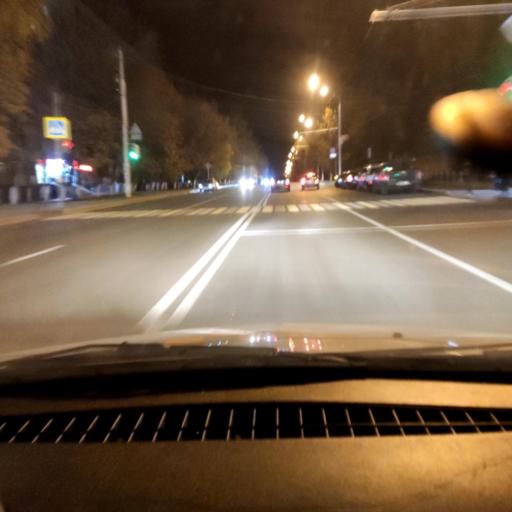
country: RU
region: Bashkortostan
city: Ufa
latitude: 54.6957
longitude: 55.9974
